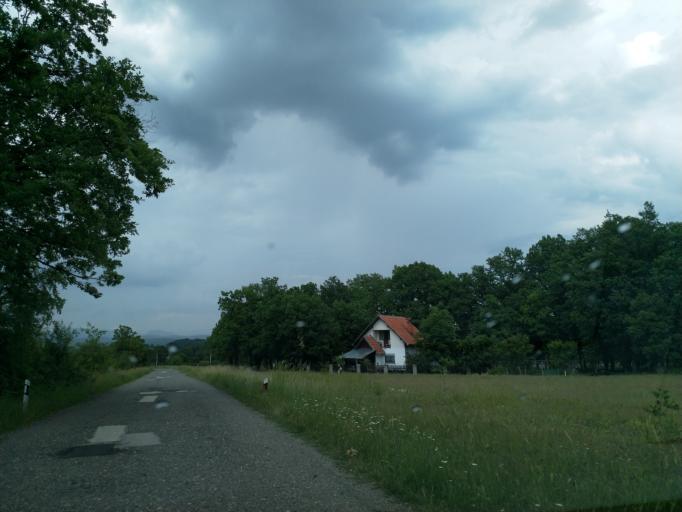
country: RS
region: Central Serbia
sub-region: Zajecarski Okrug
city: Boljevac
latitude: 43.9670
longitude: 21.9680
